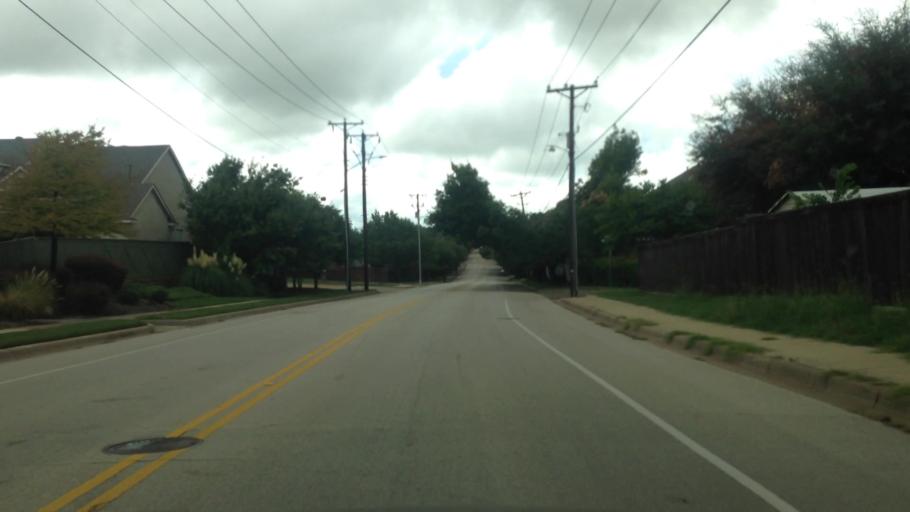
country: US
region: Texas
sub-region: Tarrant County
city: Crowley
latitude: 32.6282
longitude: -97.3999
